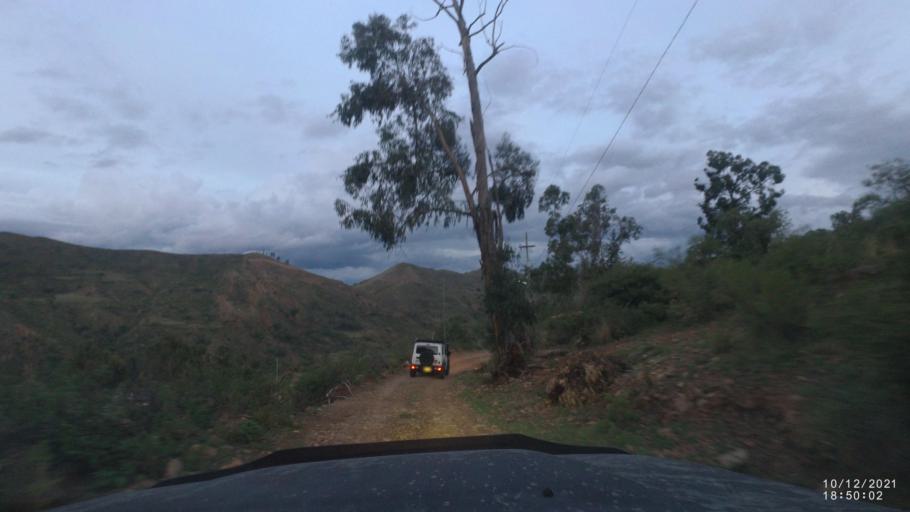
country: BO
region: Cochabamba
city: Tarata
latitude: -17.8813
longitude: -65.9697
